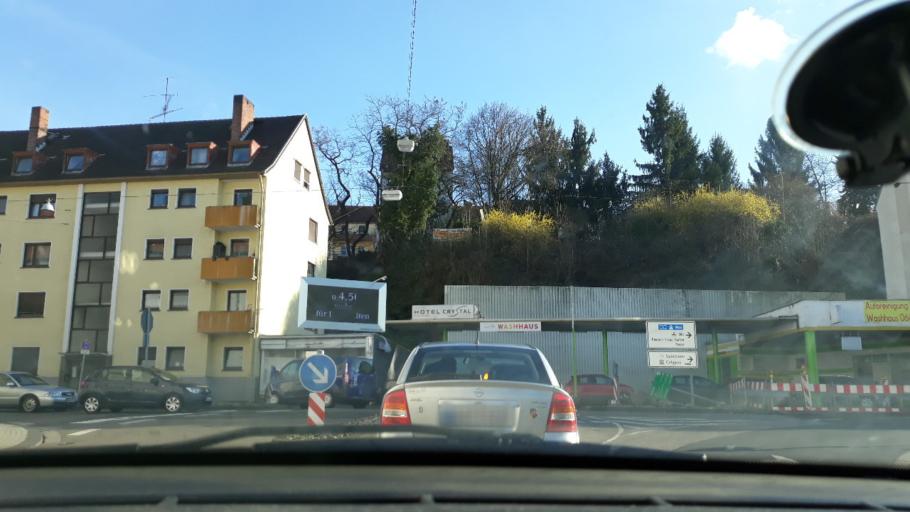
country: DE
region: Saarland
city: Saarbrucken
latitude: 49.2328
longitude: 6.9725
